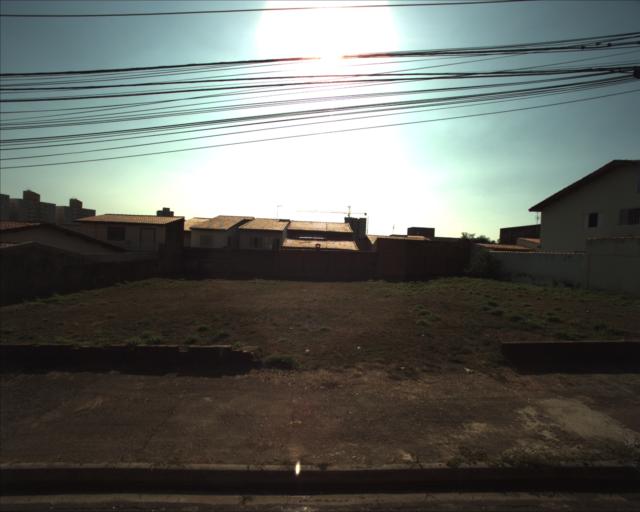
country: BR
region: Sao Paulo
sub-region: Sorocaba
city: Sorocaba
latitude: -23.4986
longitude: -47.4260
